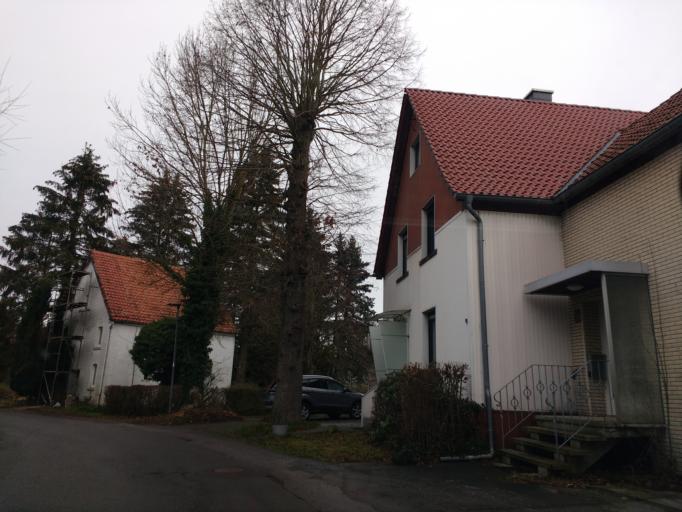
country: DE
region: North Rhine-Westphalia
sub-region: Regierungsbezirk Detmold
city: Horn
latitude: 51.8549
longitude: 8.9599
